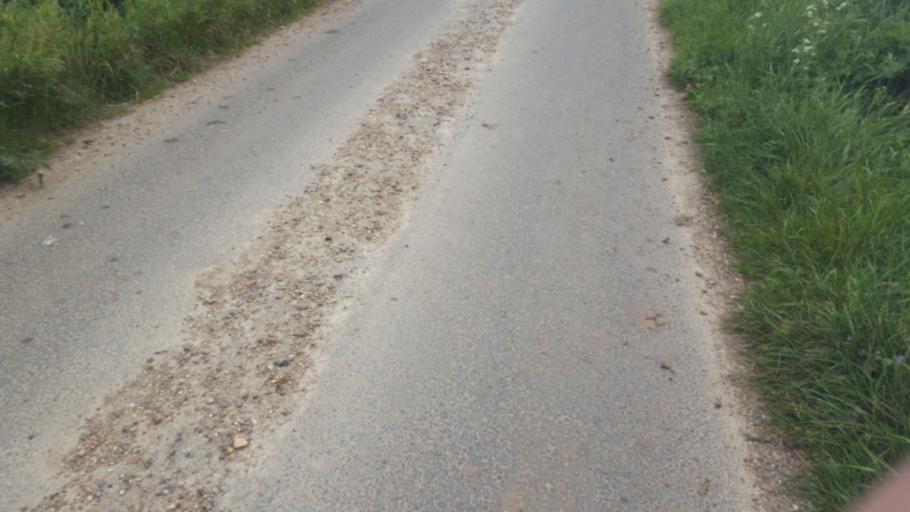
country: GB
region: England
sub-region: Essex
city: Saint Osyth
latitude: 51.7915
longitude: 1.0660
